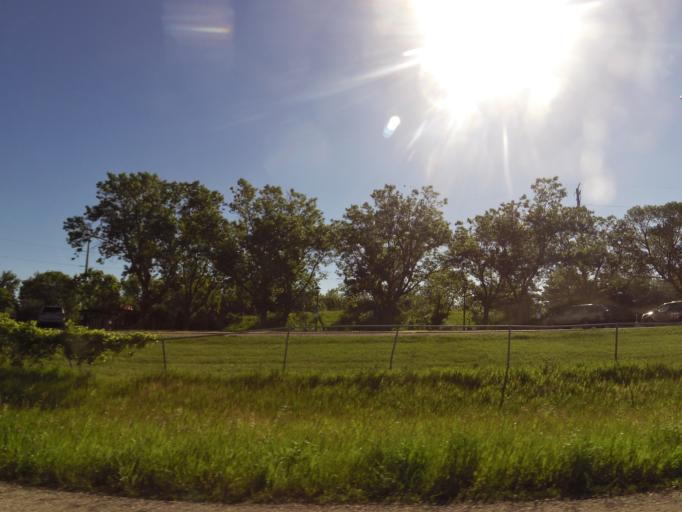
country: US
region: Minnesota
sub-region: Grant County
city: Elbow Lake
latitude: 46.1330
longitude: -95.9229
